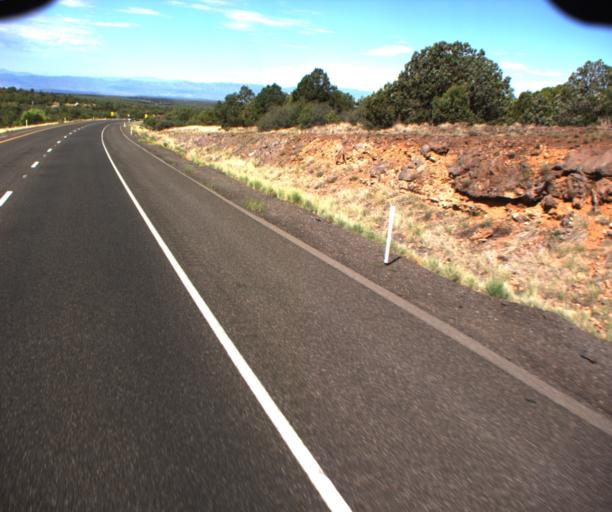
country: US
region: Arizona
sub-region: Yavapai County
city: Village of Oak Creek (Big Park)
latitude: 34.7845
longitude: -111.6100
